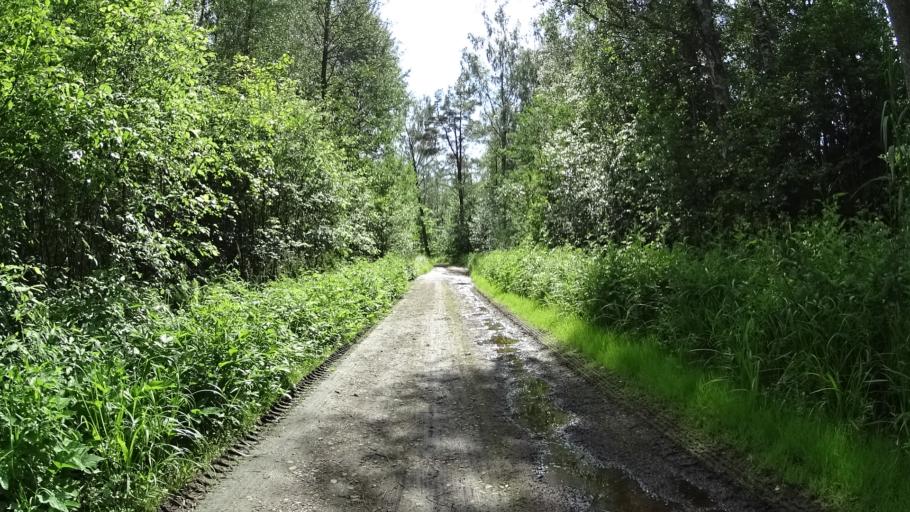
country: FI
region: Uusimaa
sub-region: Raaseporin
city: Pohja
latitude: 60.1055
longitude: 23.5476
